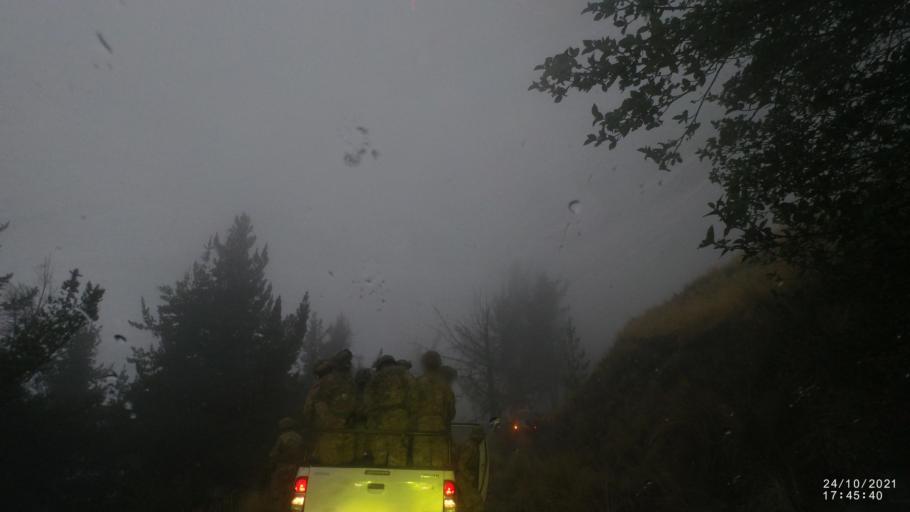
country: BO
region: Cochabamba
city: Cochabamba
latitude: -17.3151
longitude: -66.1346
